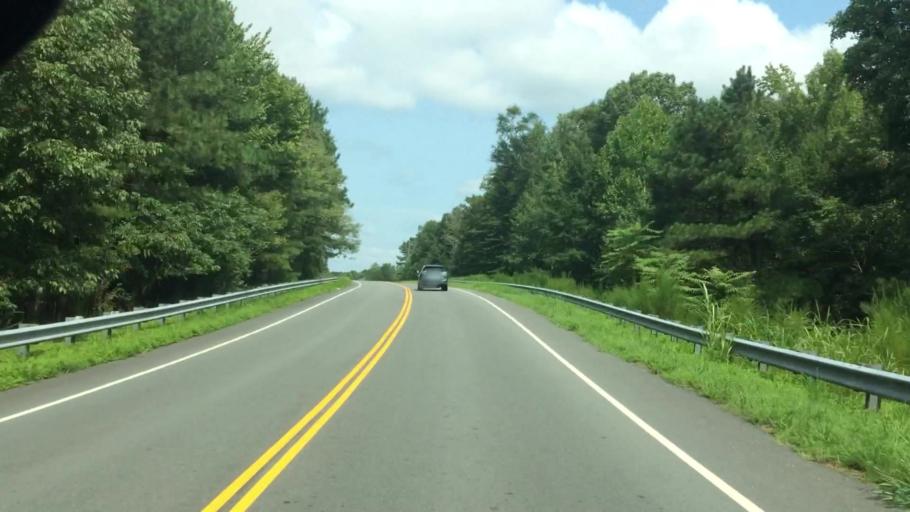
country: US
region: Virginia
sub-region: James City County
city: Williamsburg
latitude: 37.2600
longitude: -76.7882
